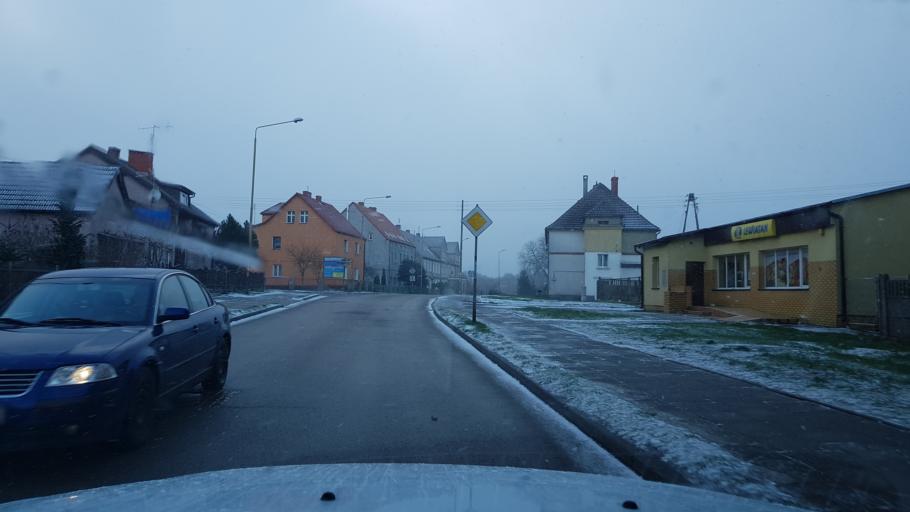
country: PL
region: West Pomeranian Voivodeship
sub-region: Powiat gryficki
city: Trzebiatow
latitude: 54.0581
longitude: 15.2796
